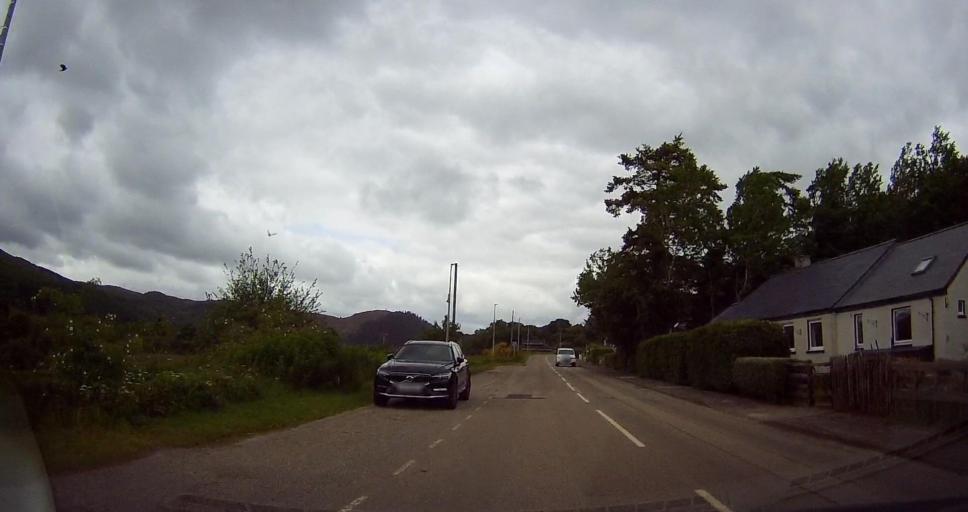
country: GB
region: Scotland
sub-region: Highland
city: Dornoch
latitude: 57.9868
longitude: -4.1532
